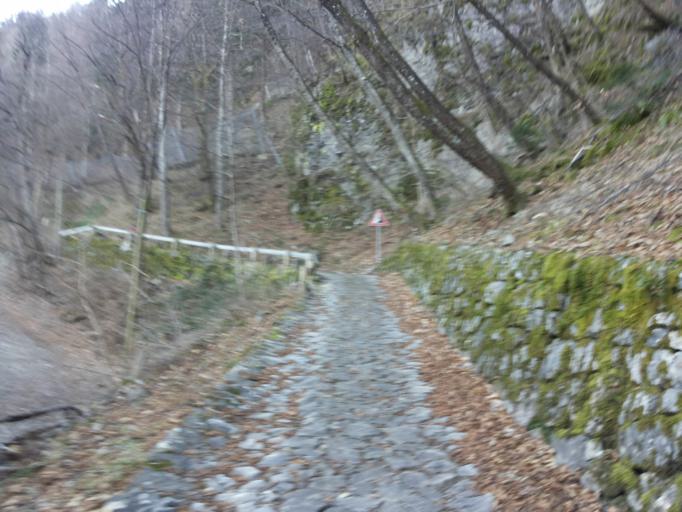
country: IT
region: Trentino-Alto Adige
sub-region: Provincia di Trento
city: Vignola
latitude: 46.0696
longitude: 11.2661
